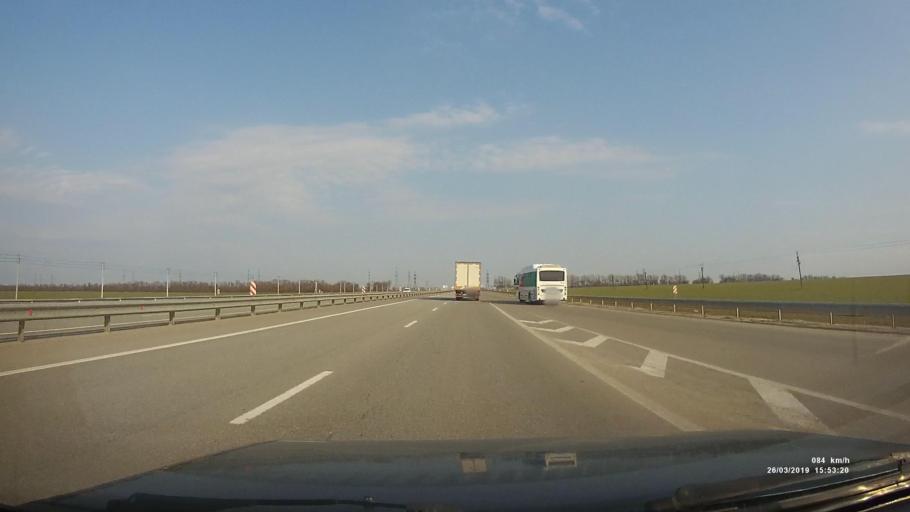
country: RU
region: Rostov
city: Krym
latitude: 47.2721
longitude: 39.5413
